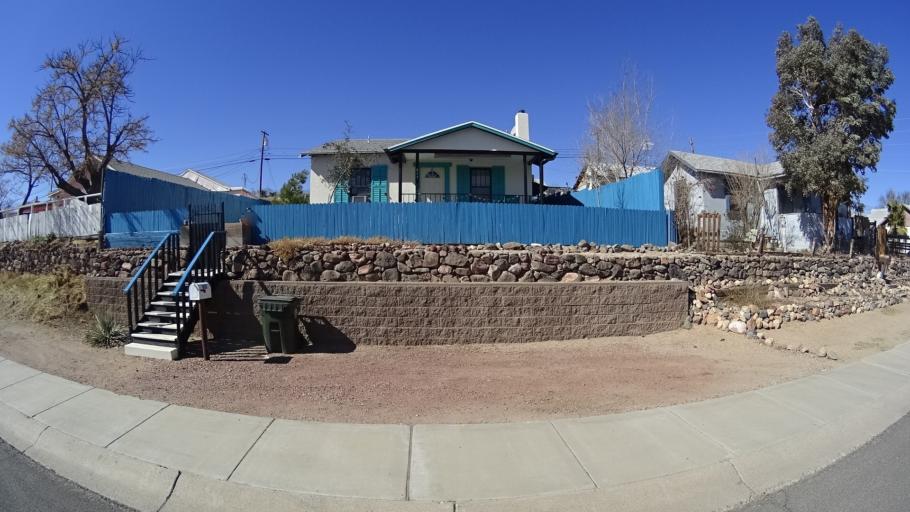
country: US
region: Arizona
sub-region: Mohave County
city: Kingman
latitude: 35.1943
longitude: -114.0614
